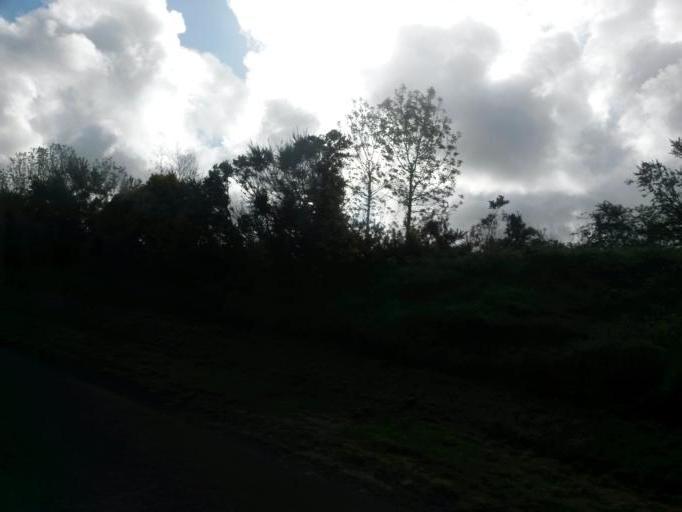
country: IE
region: Leinster
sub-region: Loch Garman
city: Gorey
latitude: 52.6437
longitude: -6.3345
